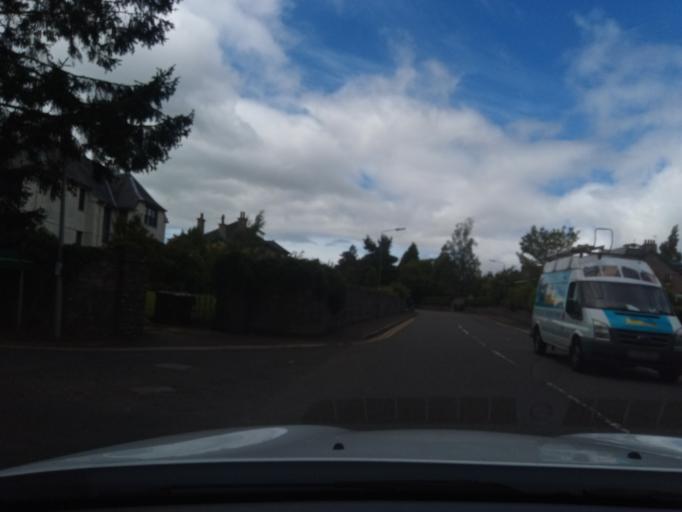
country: GB
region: Scotland
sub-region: Stirling
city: Dunblane
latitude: 56.1902
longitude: -3.9738
